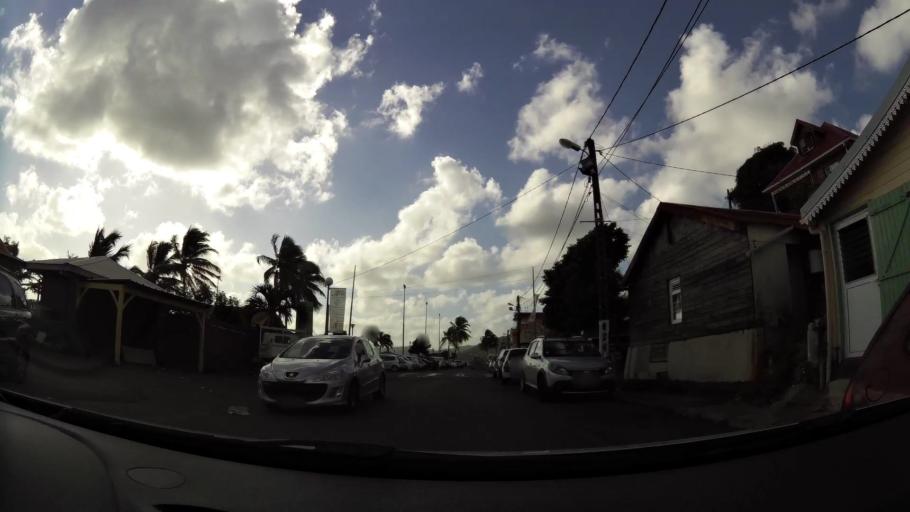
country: MQ
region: Martinique
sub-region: Martinique
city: Le Robert
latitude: 14.6791
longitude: -60.9381
